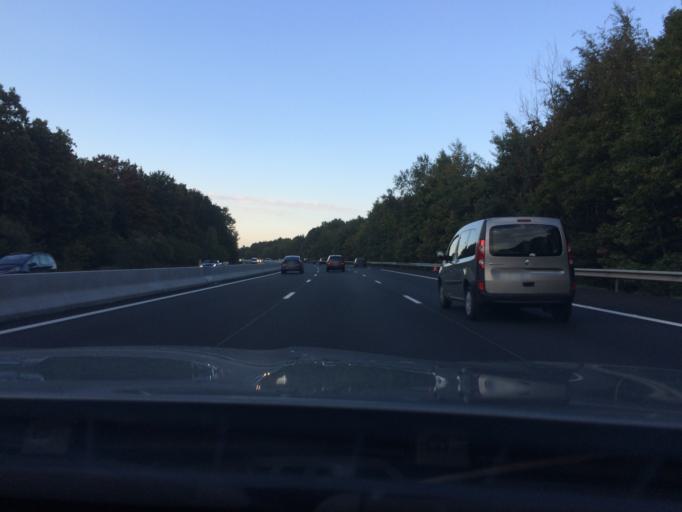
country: FR
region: Ile-de-France
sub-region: Departement de l'Essonne
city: Soisy-sur-Ecole
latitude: 48.5015
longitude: 2.5129
